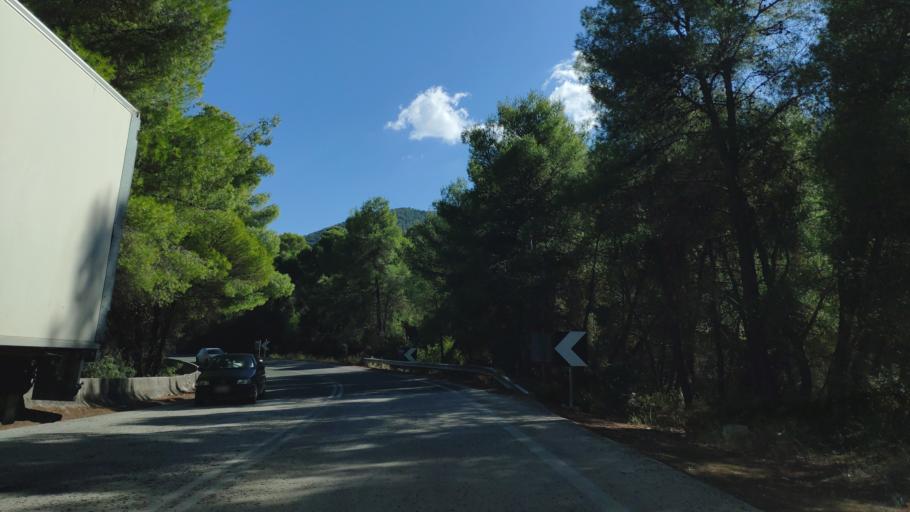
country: GR
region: Peloponnese
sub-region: Nomos Korinthias
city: Sofikon
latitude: 37.8292
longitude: 23.0309
